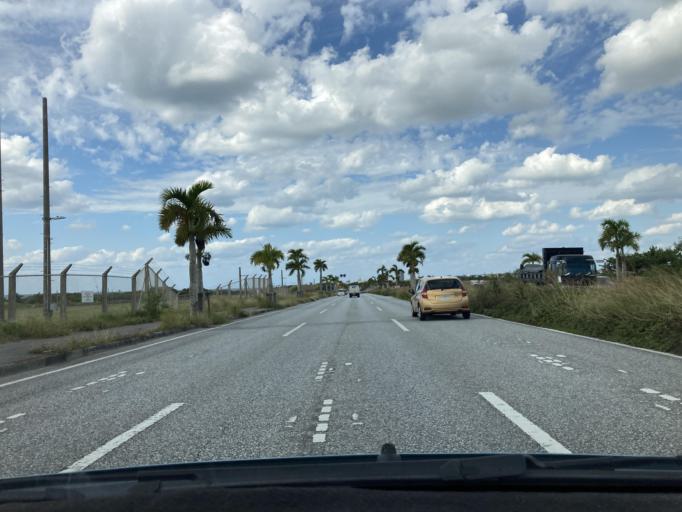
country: JP
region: Okinawa
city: Chatan
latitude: 26.3392
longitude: 127.7507
